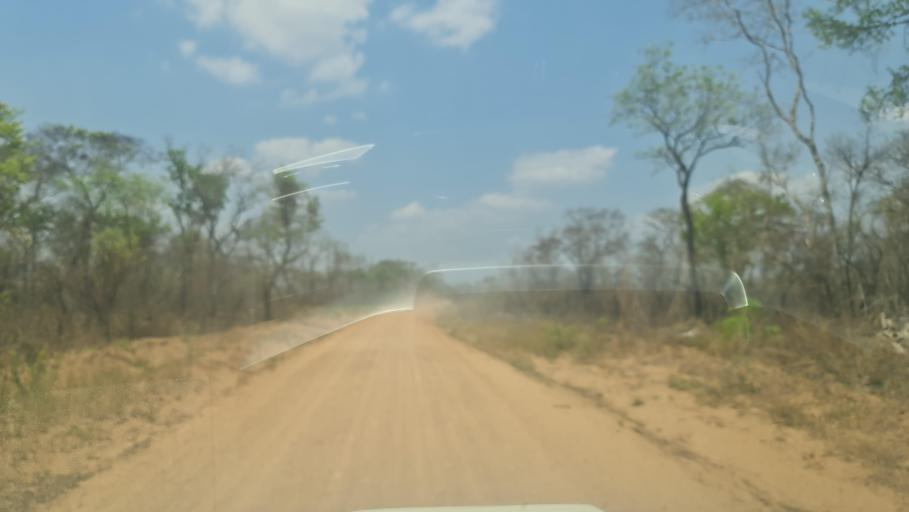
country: MW
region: Southern Region
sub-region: Nsanje District
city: Nsanje
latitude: -17.5620
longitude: 35.9006
